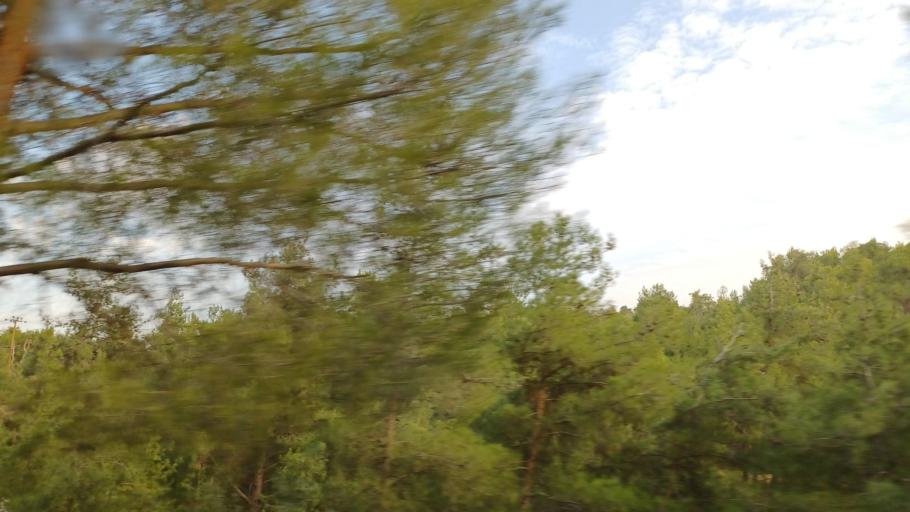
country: CY
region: Lefkosia
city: Kakopetria
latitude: 35.0533
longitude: 32.9096
